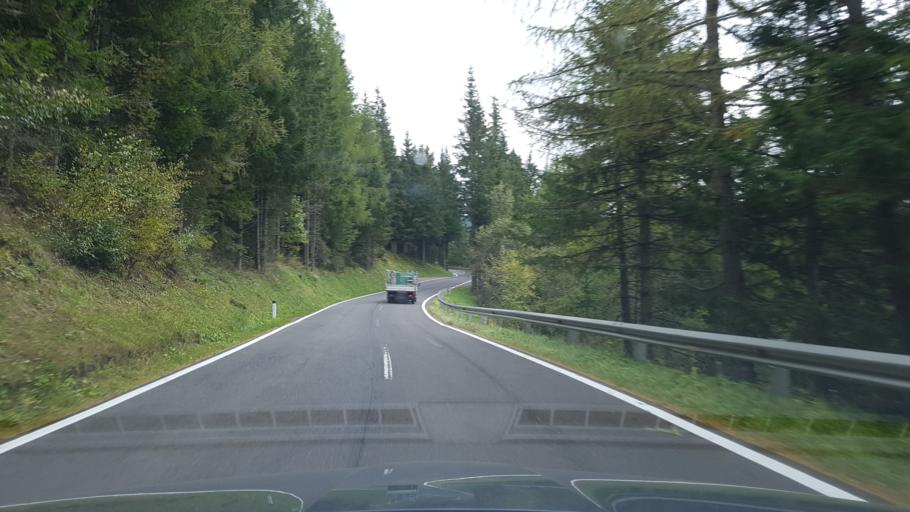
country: AT
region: Styria
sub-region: Politischer Bezirk Murtal
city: Kleinlobming
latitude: 47.1236
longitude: 14.8879
